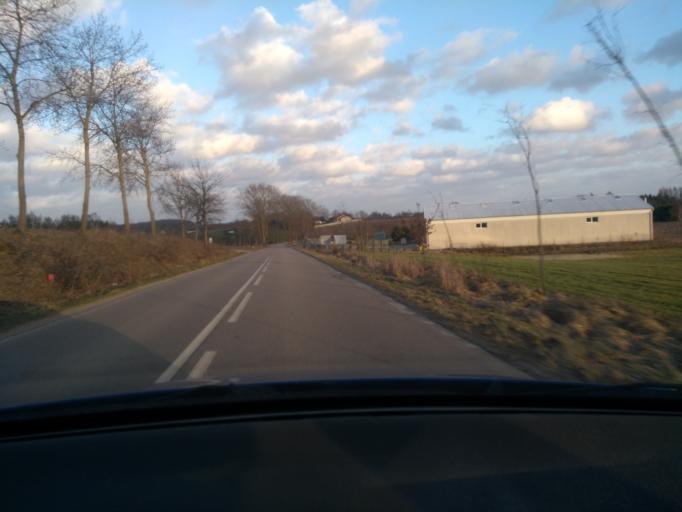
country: PL
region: Pomeranian Voivodeship
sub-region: Powiat kartuski
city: Przodkowo
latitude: 54.4164
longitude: 18.2984
